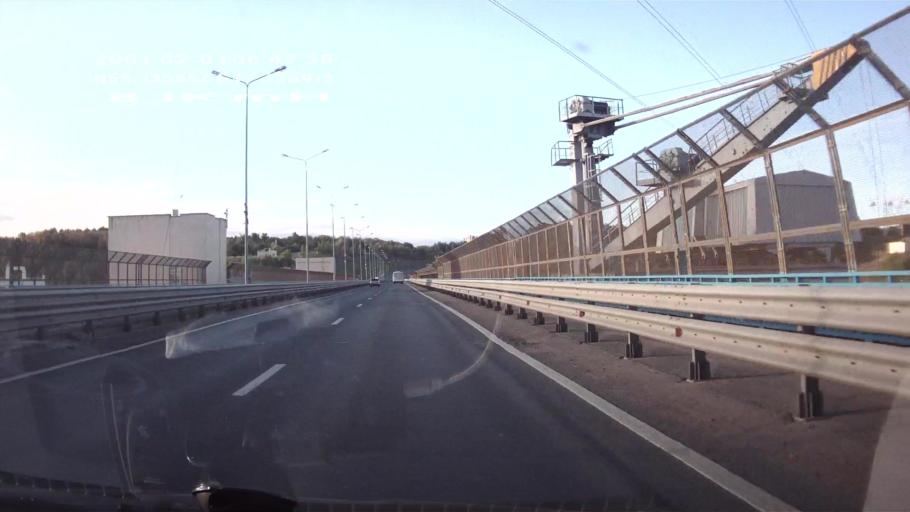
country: RU
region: Chuvashia
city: Novocheboksarsk
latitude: 56.1371
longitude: 47.4656
